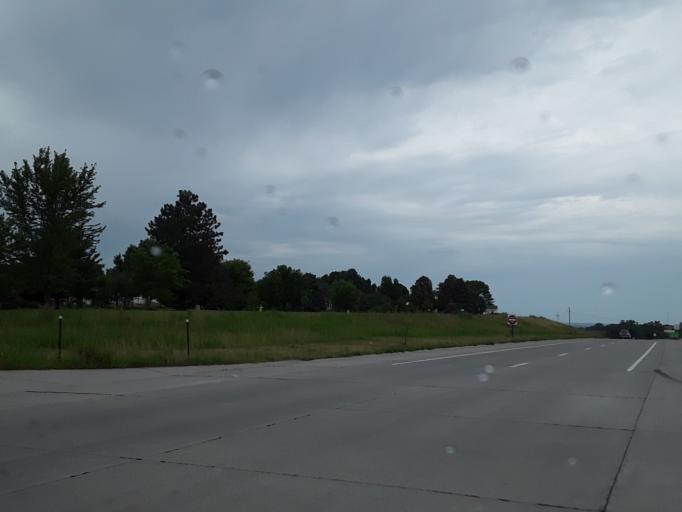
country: US
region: Nebraska
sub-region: Washington County
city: Blair
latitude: 41.5017
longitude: -96.1472
